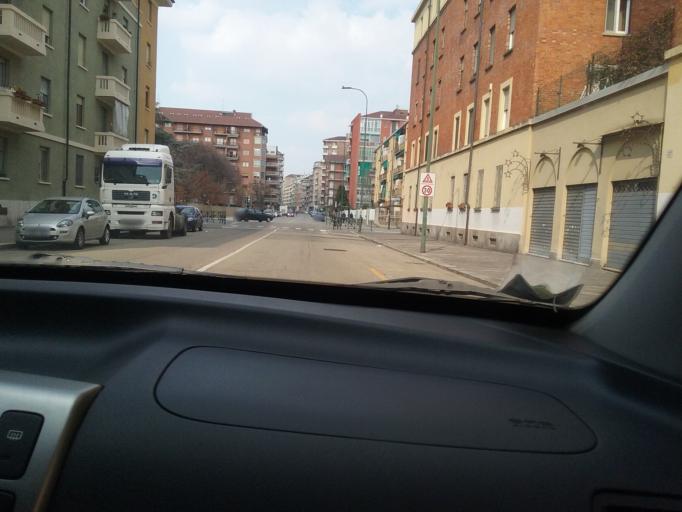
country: IT
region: Piedmont
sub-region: Provincia di Torino
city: Gerbido
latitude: 45.0332
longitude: 7.6389
